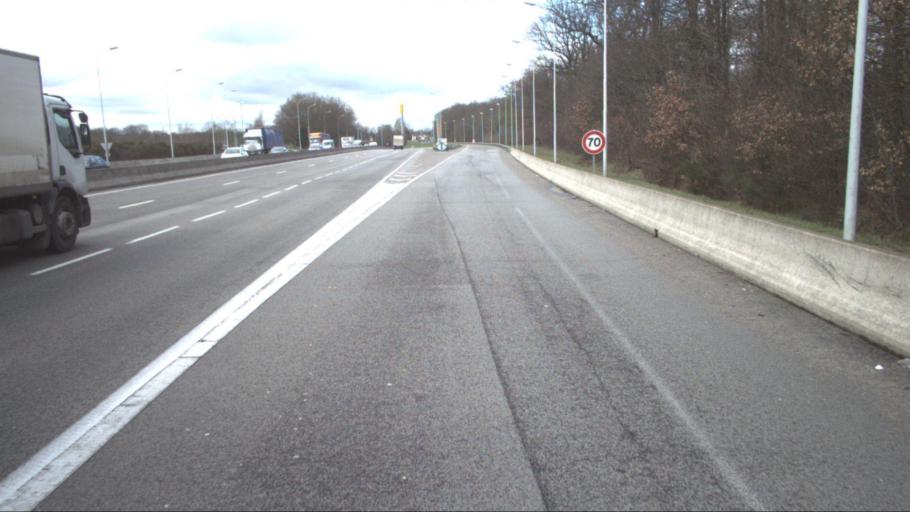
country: FR
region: Ile-de-France
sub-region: Departement des Yvelines
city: Saint-Cyr-l'Ecole
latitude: 48.7932
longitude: 2.0831
